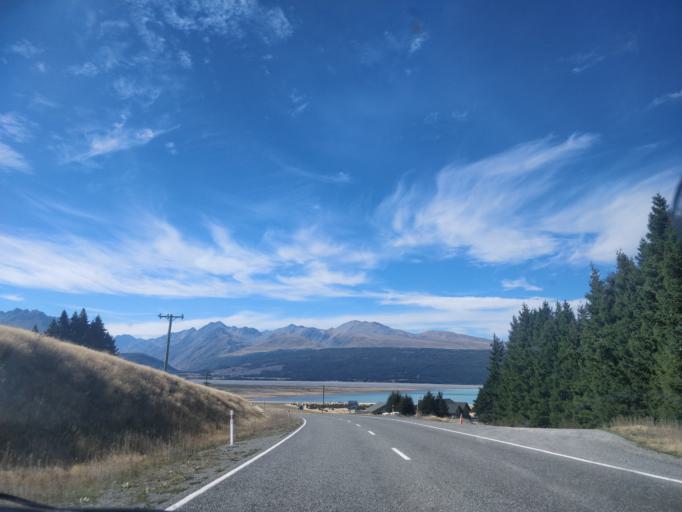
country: NZ
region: Canterbury
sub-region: Timaru District
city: Pleasant Point
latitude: -43.9128
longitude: 170.1188
